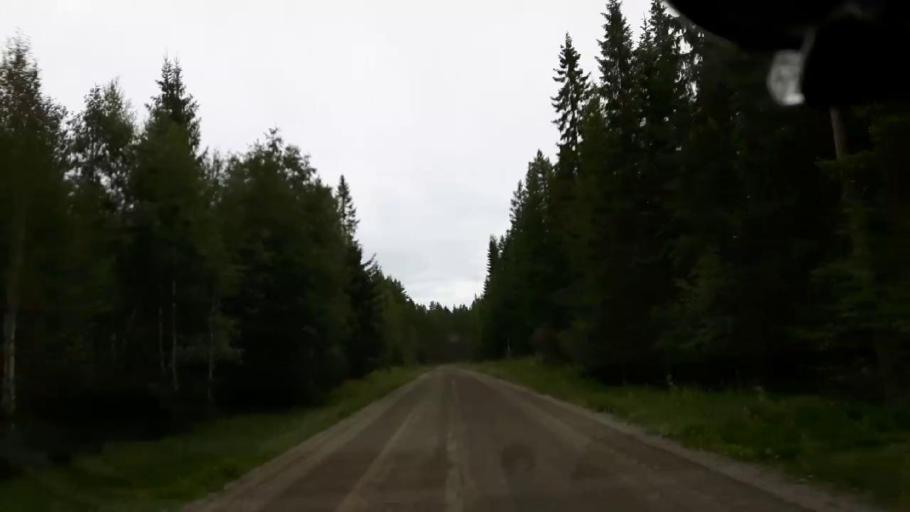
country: SE
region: Jaemtland
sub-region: Braecke Kommun
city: Braecke
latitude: 62.9478
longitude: 15.4434
